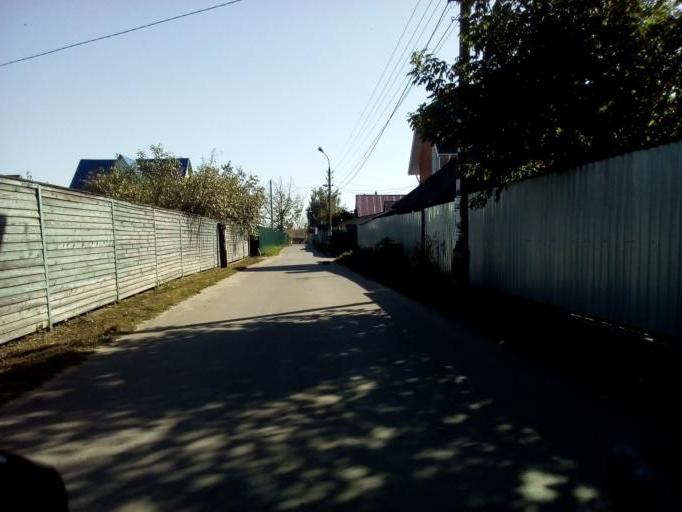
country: RU
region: Moskovskaya
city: Ramenskoye
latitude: 55.5490
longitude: 38.2853
